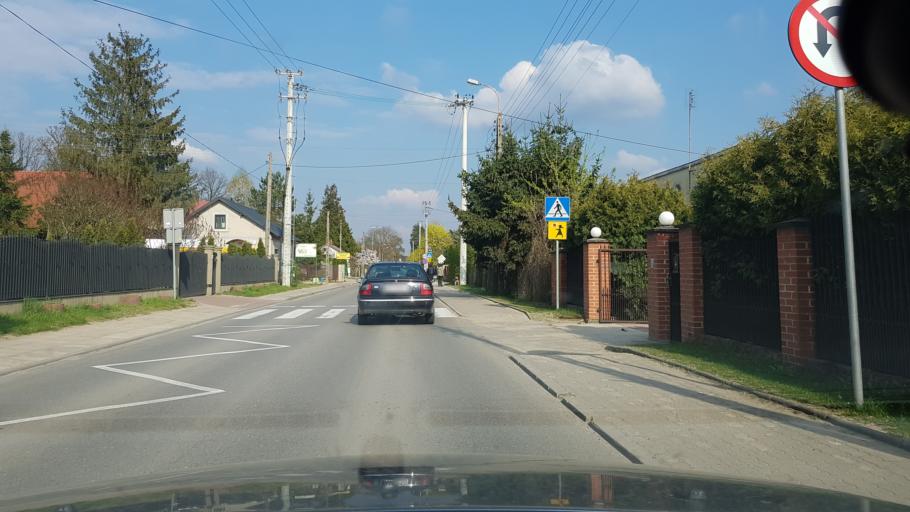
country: PL
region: Masovian Voivodeship
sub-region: Powiat otwocki
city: Jozefow
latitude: 52.1705
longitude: 21.2937
